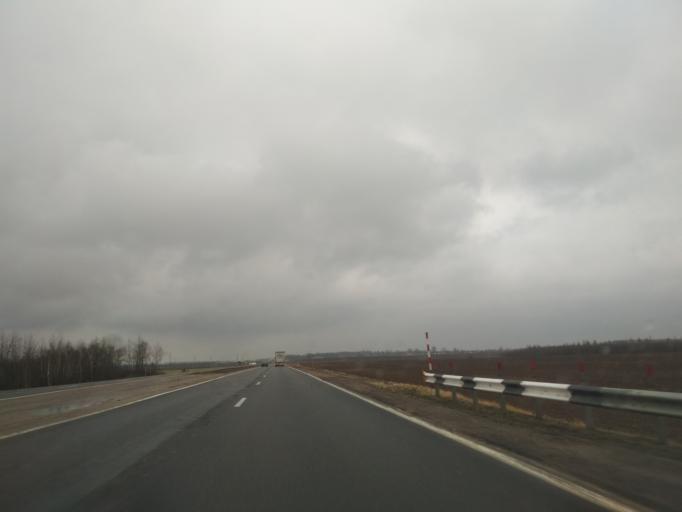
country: BY
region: Minsk
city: Dukora
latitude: 53.6458
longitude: 27.9845
